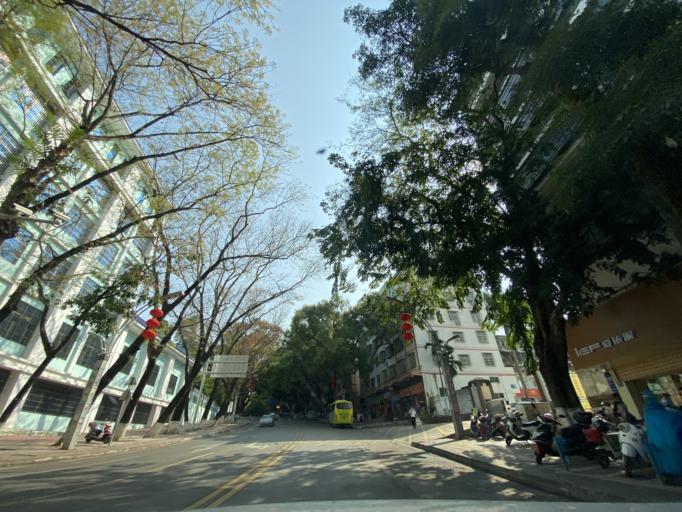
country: CN
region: Hainan
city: Chongshan
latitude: 18.7789
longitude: 109.5148
